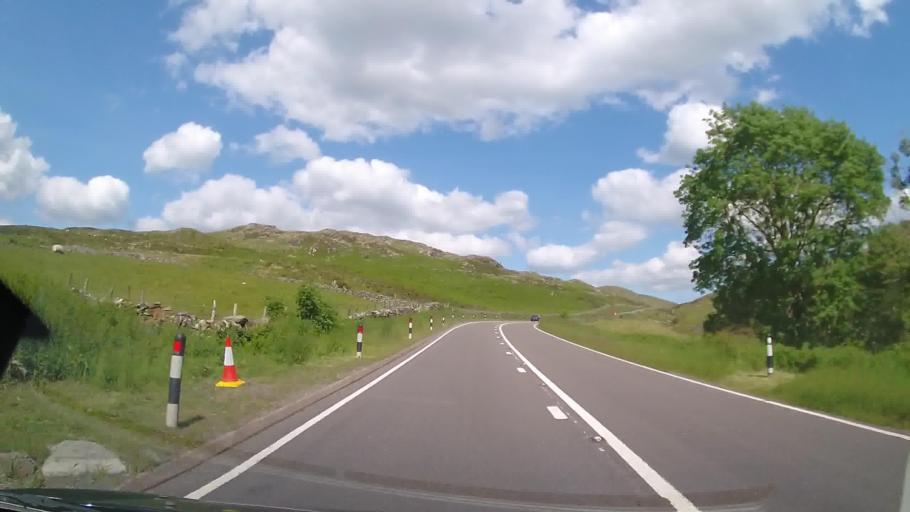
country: GB
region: Wales
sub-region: Gwynedd
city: Dolgellau
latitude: 52.7393
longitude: -3.7947
